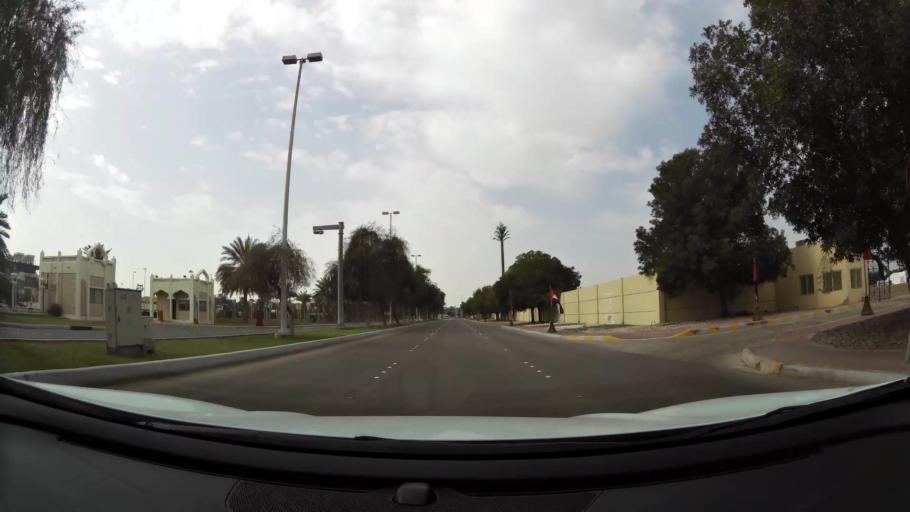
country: AE
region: Abu Dhabi
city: Abu Dhabi
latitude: 24.4456
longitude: 54.3751
